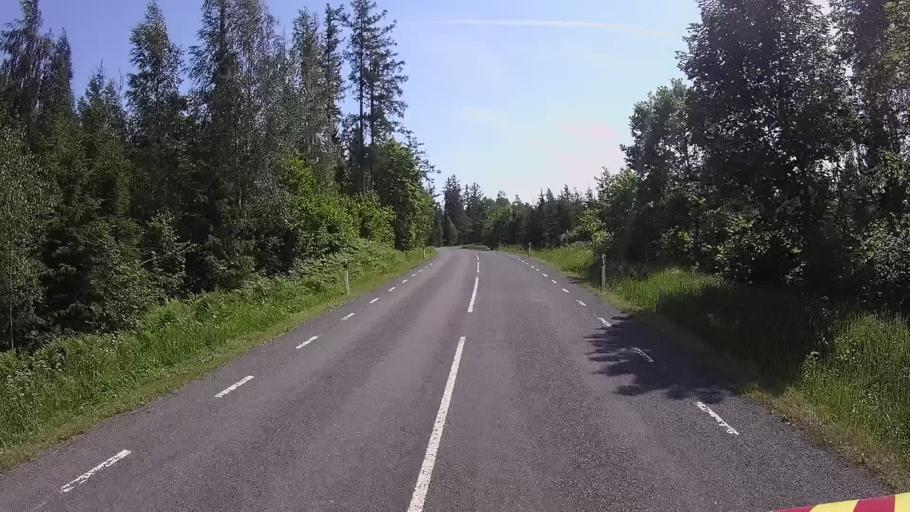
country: EE
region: Viljandimaa
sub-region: Karksi vald
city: Karksi-Nuia
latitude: 58.0806
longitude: 25.5601
